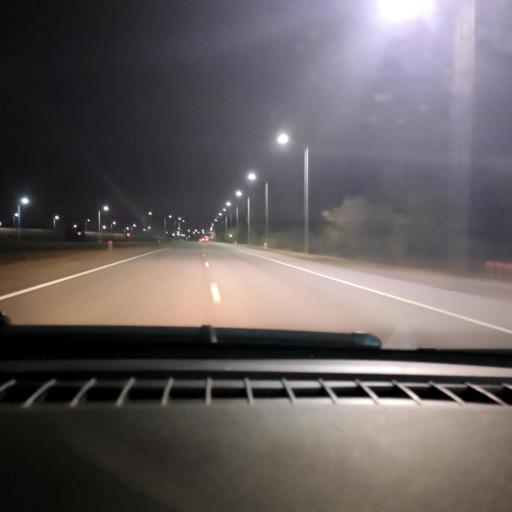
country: RU
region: Voronezj
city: Podgornoye
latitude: 51.8399
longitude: 39.2139
